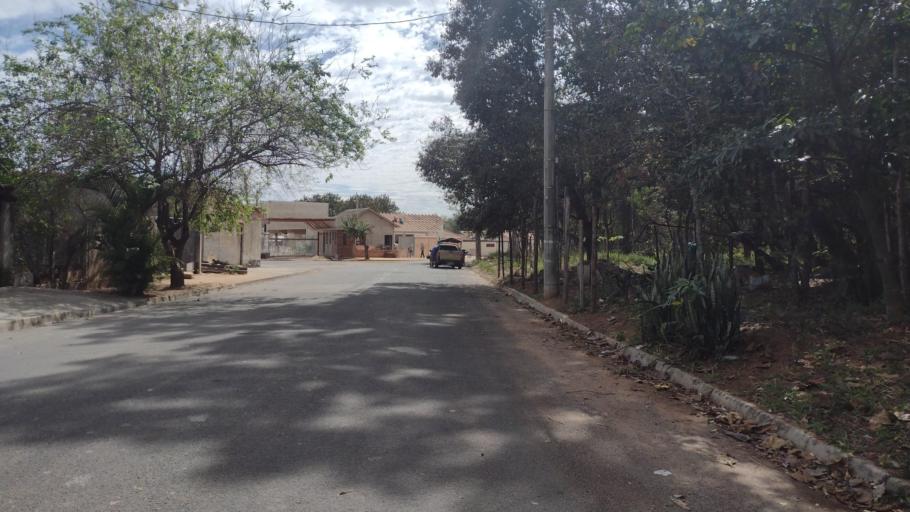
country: BR
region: Sao Paulo
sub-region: Sorocaba
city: Sorocaba
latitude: -23.4223
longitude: -47.4560
